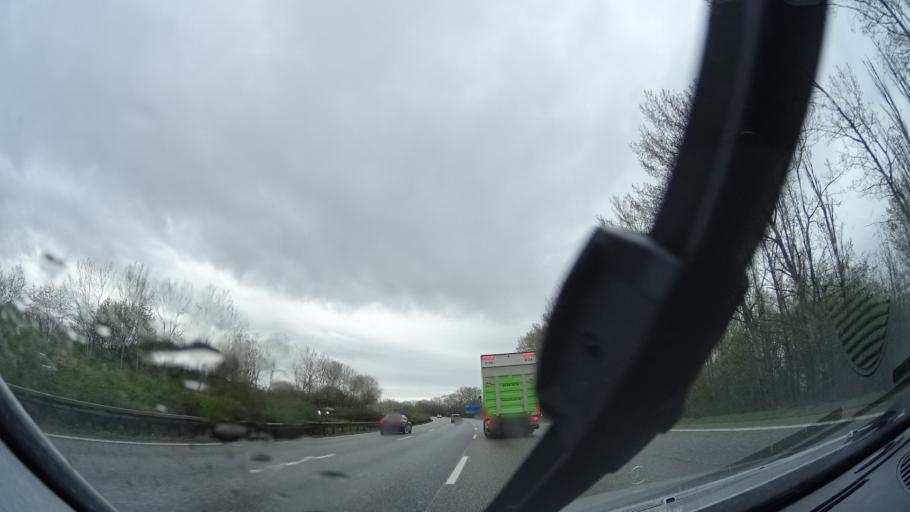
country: DK
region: Capital Region
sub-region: Hvidovre Kommune
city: Hvidovre
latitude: 55.6152
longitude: 12.4546
